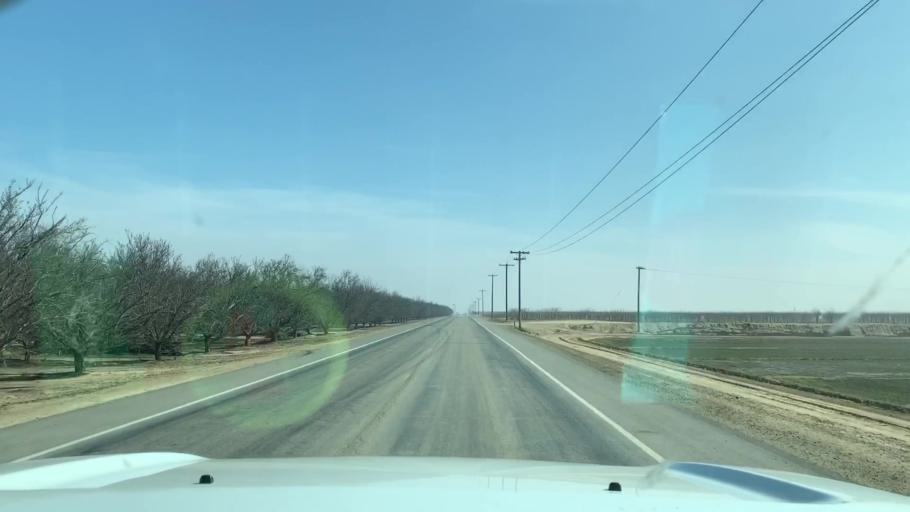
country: US
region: California
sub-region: Kern County
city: Buttonwillow
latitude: 35.4424
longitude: -119.4835
